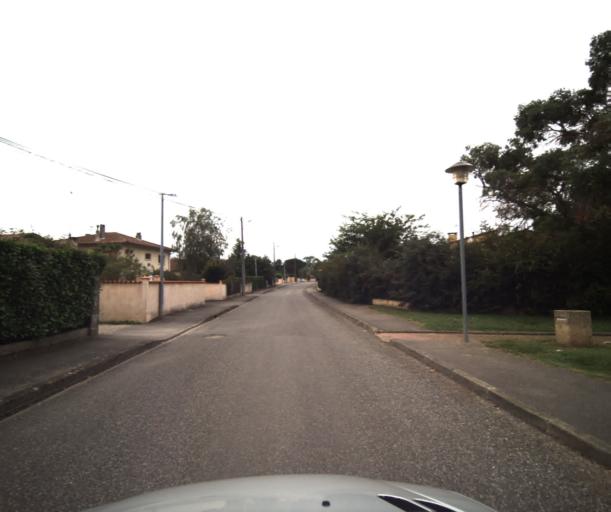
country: FR
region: Midi-Pyrenees
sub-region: Departement de la Haute-Garonne
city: Labarthe-sur-Leze
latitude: 43.4536
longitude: 1.4063
